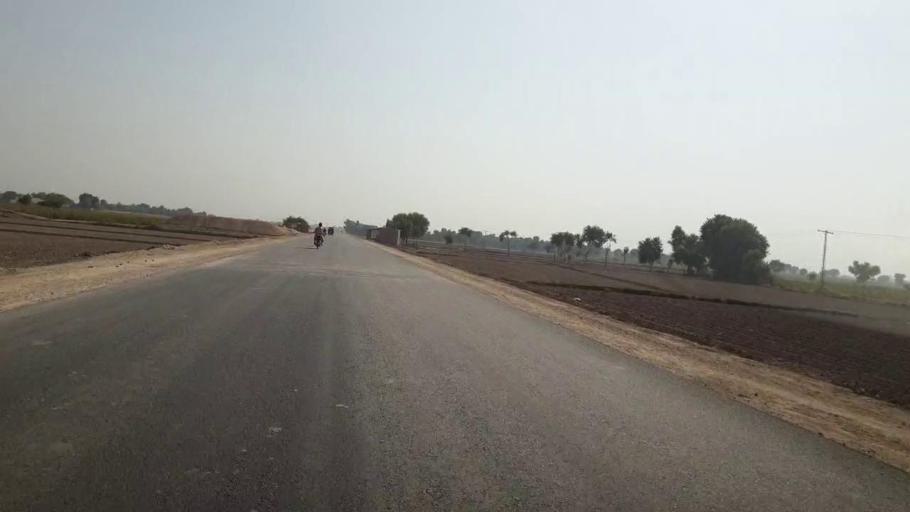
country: PK
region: Sindh
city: Dadu
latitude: 26.6545
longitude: 67.7763
